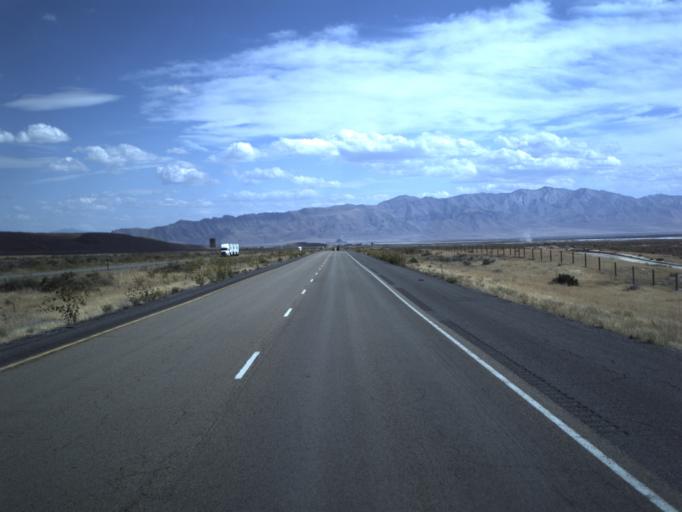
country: US
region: Utah
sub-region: Tooele County
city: Grantsville
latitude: 40.7892
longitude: -112.8300
